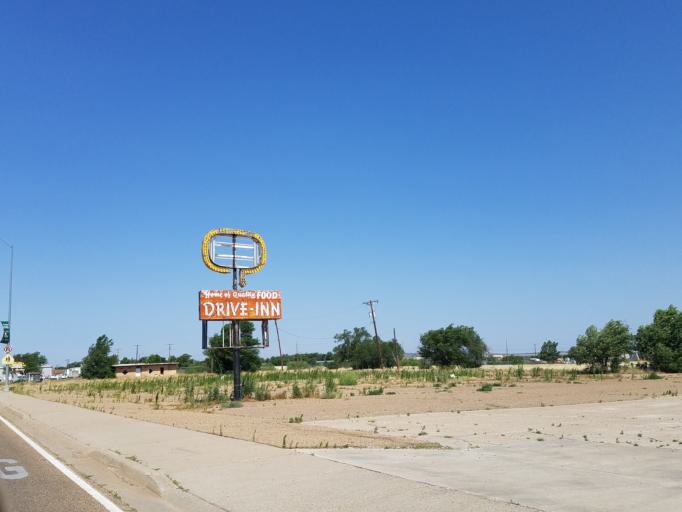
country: US
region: New Mexico
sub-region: Quay County
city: Tucumcari
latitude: 35.1696
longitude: -103.7220
